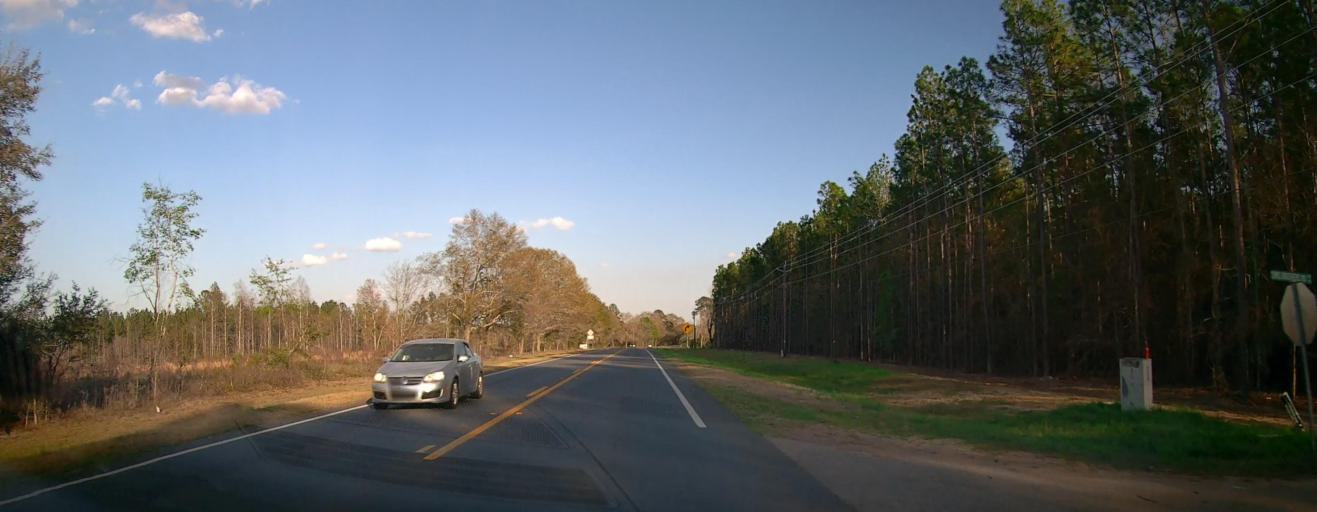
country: US
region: Georgia
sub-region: Evans County
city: Claxton
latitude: 32.1602
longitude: -81.8677
